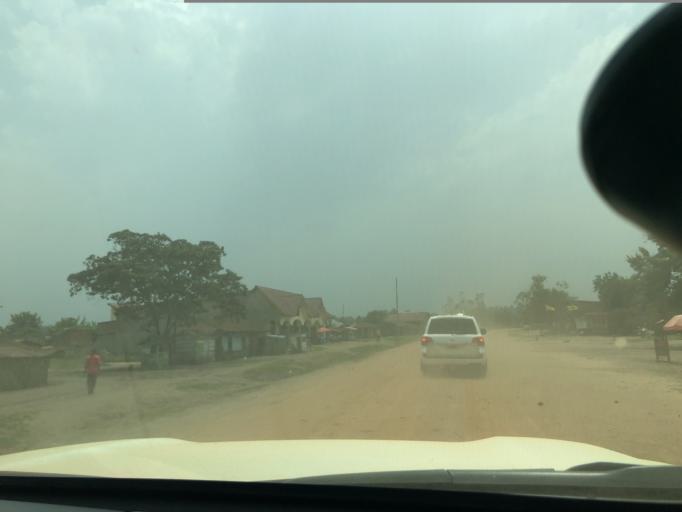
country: UG
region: Western Region
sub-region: Kasese District
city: Margherita
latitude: 0.3276
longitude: 29.6763
